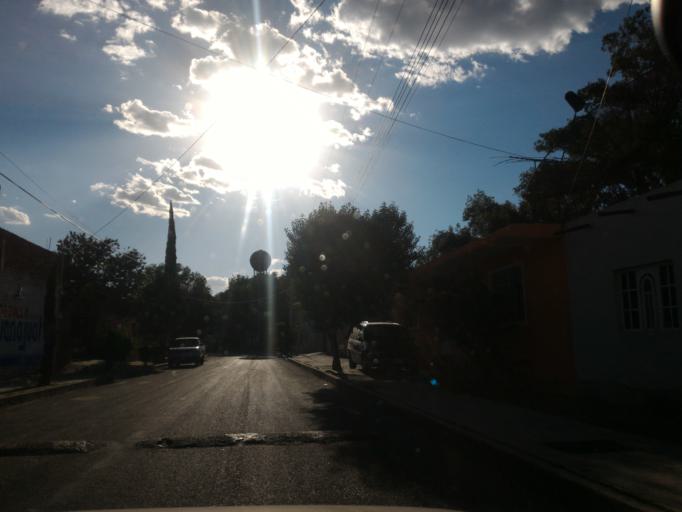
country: MX
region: Jalisco
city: San Diego de Alejandria
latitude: 20.8813
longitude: -101.9833
